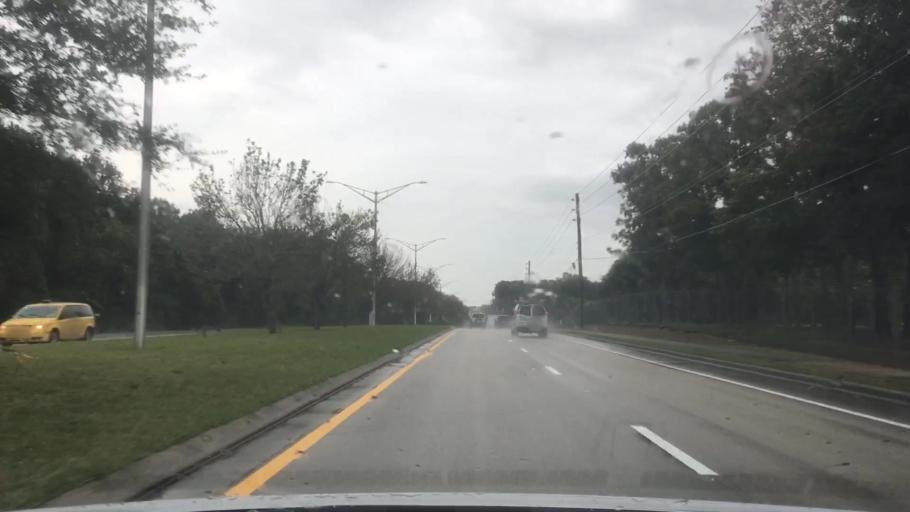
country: US
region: Florida
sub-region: Duval County
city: Atlantic Beach
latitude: 30.3487
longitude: -81.5211
